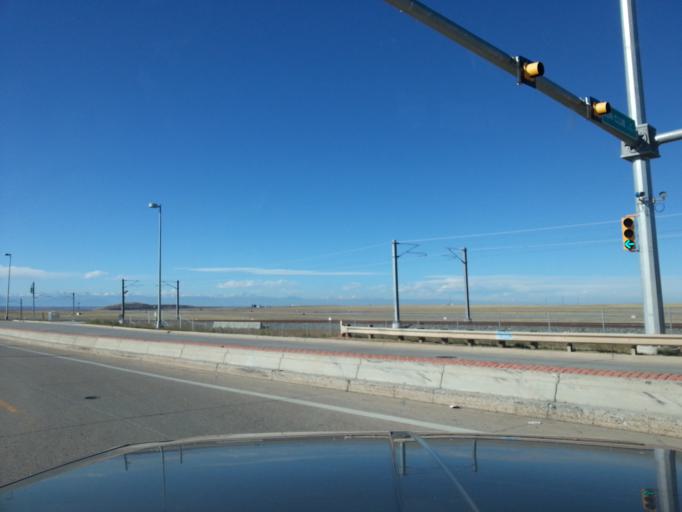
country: US
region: Colorado
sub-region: Adams County
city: Aurora
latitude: 39.8381
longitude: -104.7155
